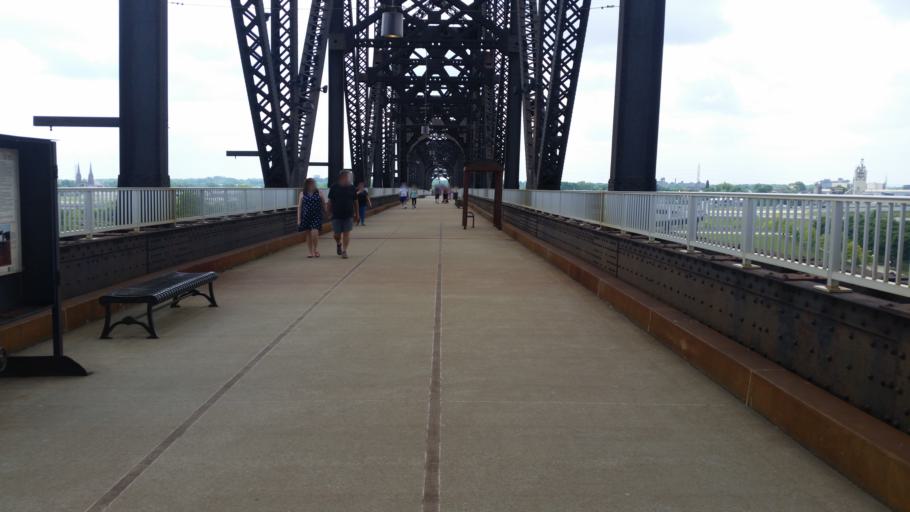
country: US
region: Indiana
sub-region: Clark County
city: Jeffersonville
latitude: 38.2647
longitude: -85.7386
